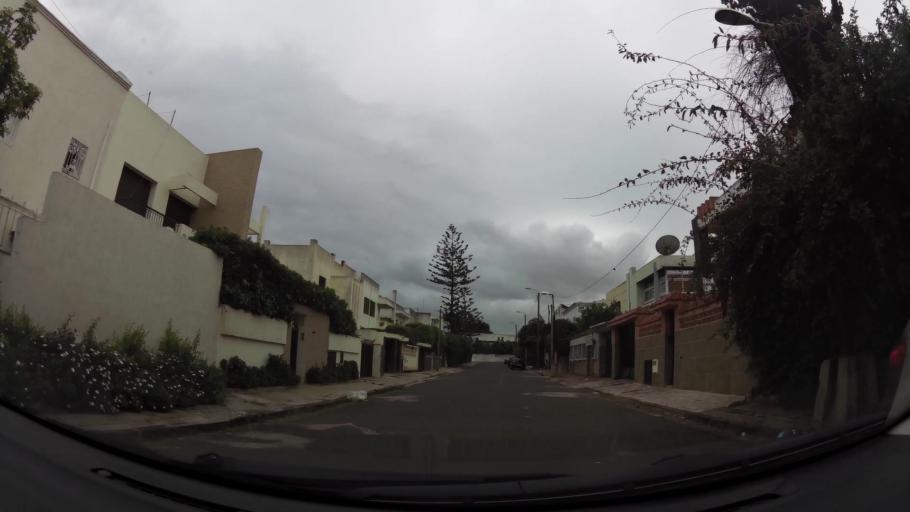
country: MA
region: Grand Casablanca
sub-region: Casablanca
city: Casablanca
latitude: 33.5943
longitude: -7.6475
